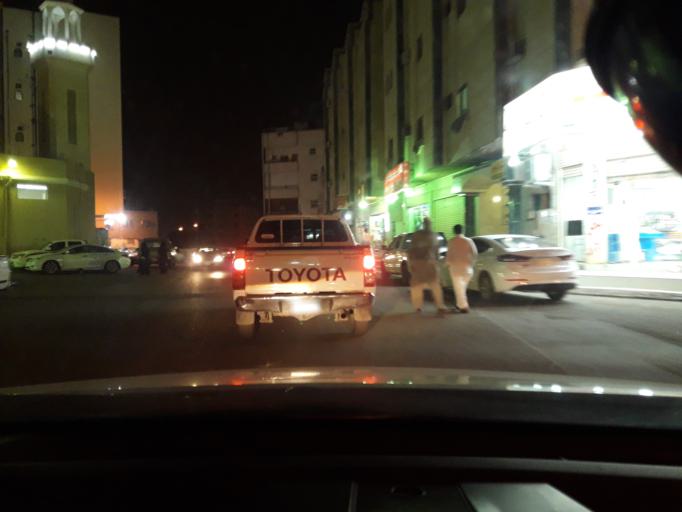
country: SA
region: Al Madinah al Munawwarah
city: Medina
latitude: 24.4670
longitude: 39.6277
